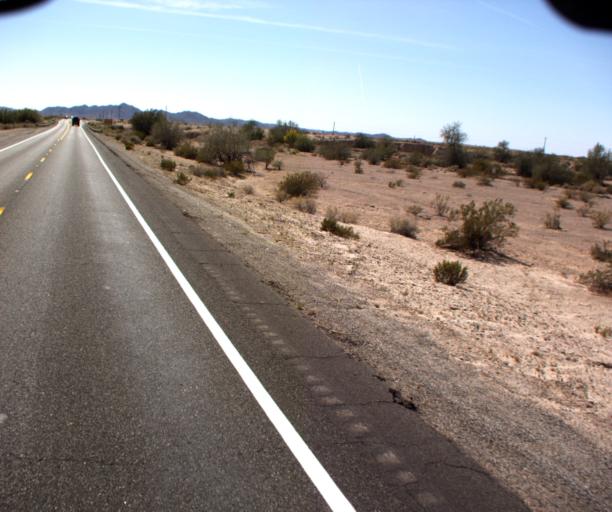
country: US
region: Arizona
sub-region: Yuma County
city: Fortuna Foothills
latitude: 32.8612
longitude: -114.3588
